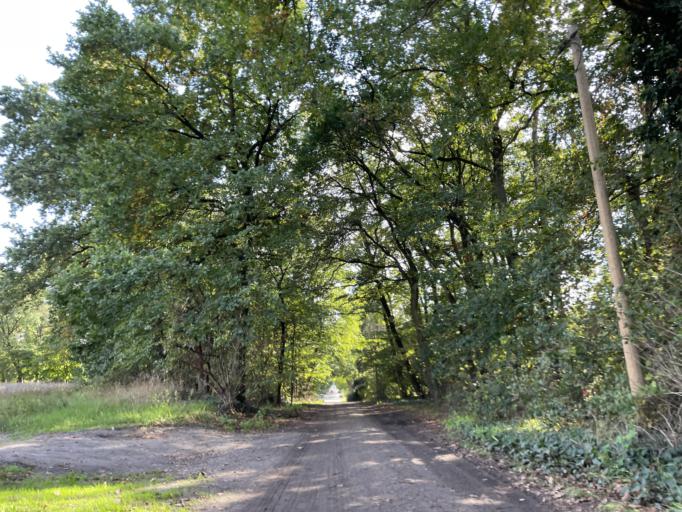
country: DE
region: Lower Saxony
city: Deutsch Evern
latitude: 53.2082
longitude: 10.4379
